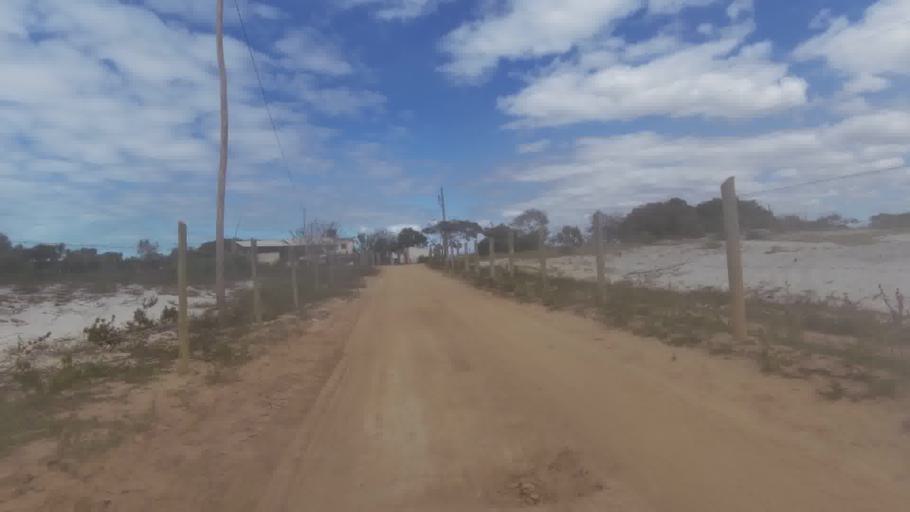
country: BR
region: Espirito Santo
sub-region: Marataizes
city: Marataizes
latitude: -21.2370
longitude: -40.9931
